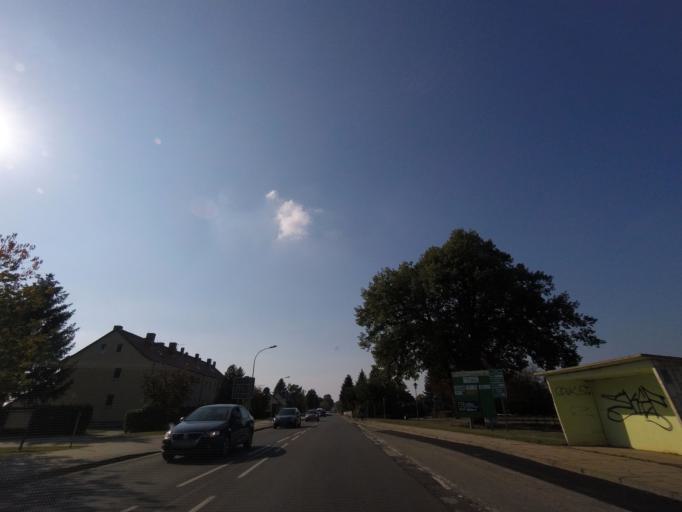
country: DE
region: Saxony-Anhalt
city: Jessen
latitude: 51.7964
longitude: 13.0161
